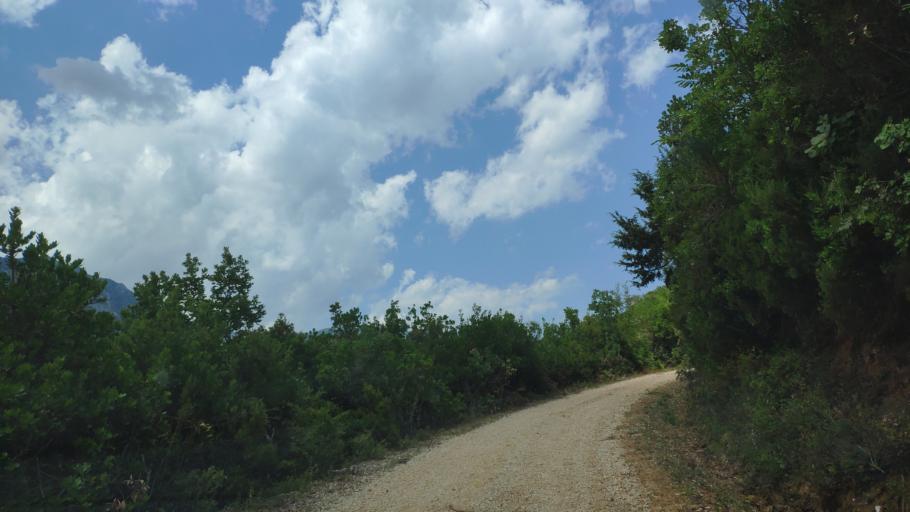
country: GR
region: Epirus
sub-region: Nomos Artas
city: Agios Dimitrios
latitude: 39.3170
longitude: 21.0107
